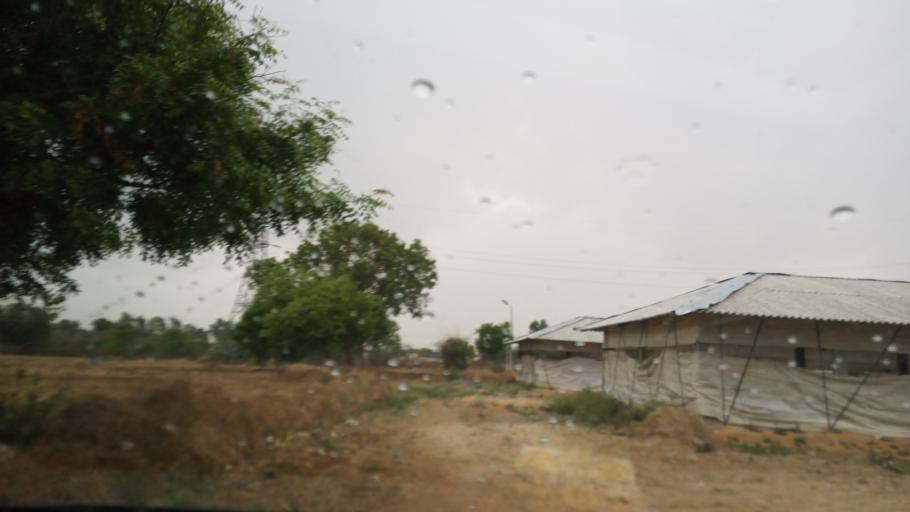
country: IN
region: Karnataka
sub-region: Kolar
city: Mulbagal
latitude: 13.1020
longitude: 78.3219
